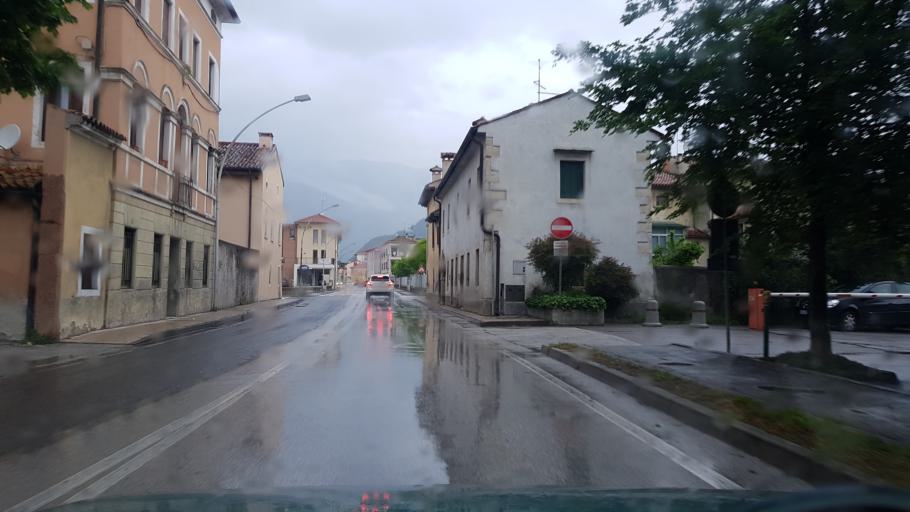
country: IT
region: Veneto
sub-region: Provincia di Treviso
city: Vittorio Veneto
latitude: 45.9798
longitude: 12.3059
